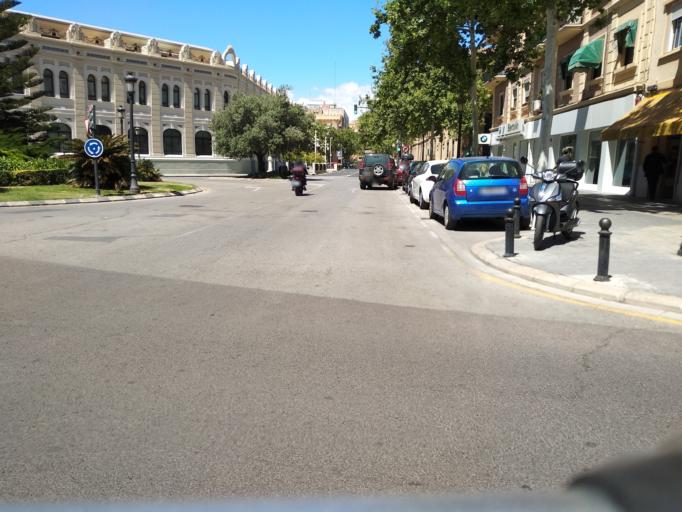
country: ES
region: Valencia
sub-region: Provincia de Valencia
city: Valencia
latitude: 39.4732
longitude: -0.3601
